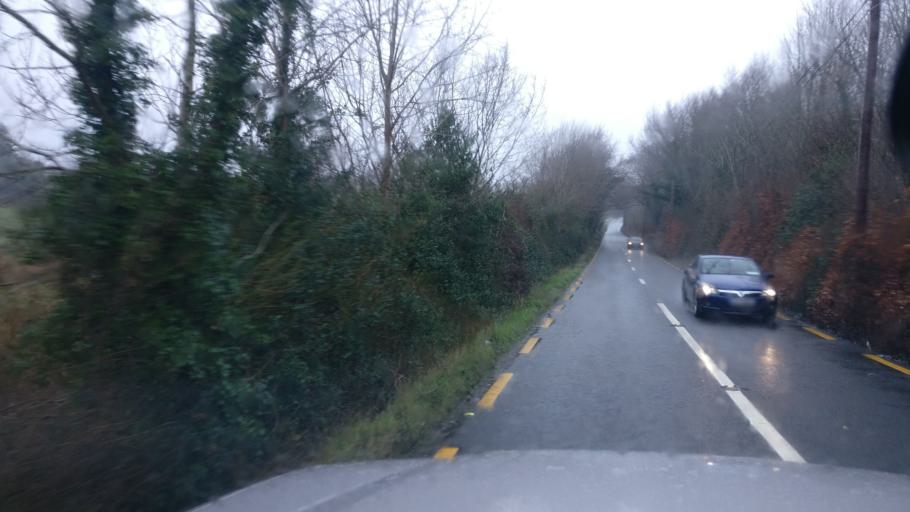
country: IE
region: Connaught
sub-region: County Galway
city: Loughrea
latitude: 53.1358
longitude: -8.4638
